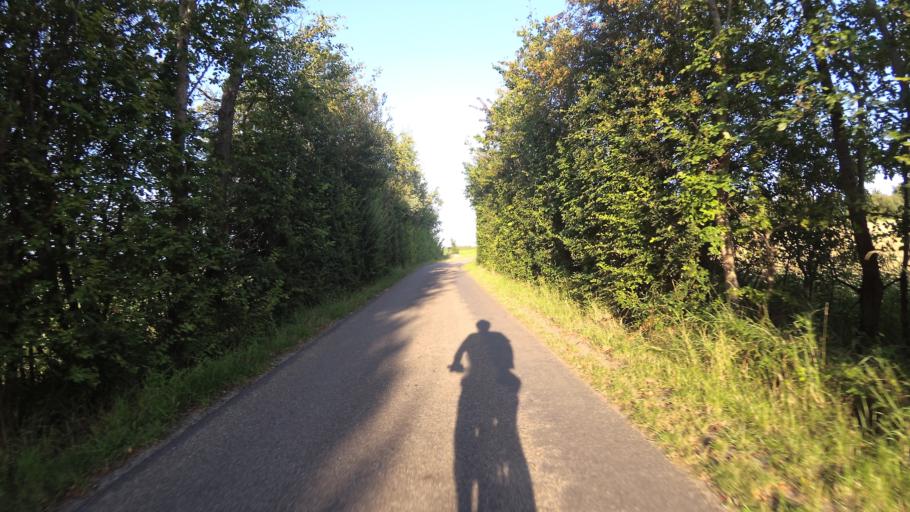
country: NL
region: Zeeland
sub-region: Gemeente Middelburg
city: Middelburg
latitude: 51.5697
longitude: 3.5867
